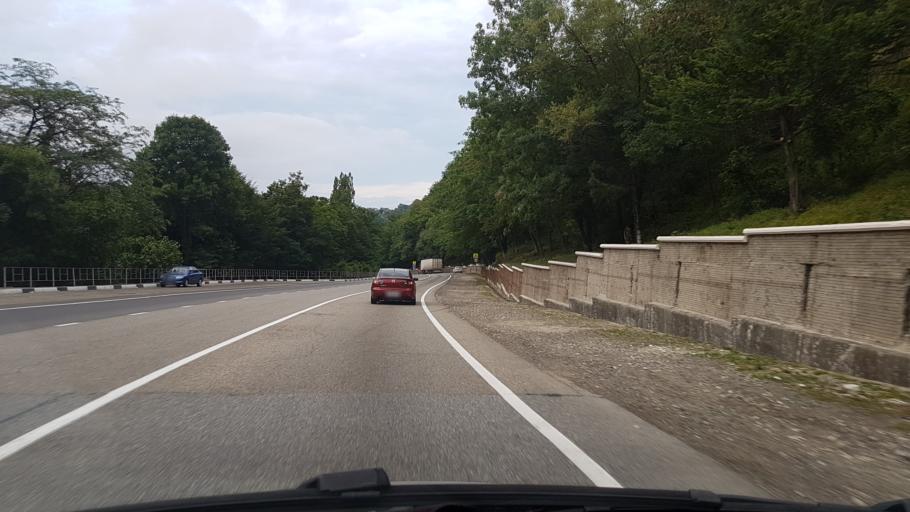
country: RU
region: Krasnodarskiy
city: Tuapse
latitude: 44.1162
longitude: 39.0553
